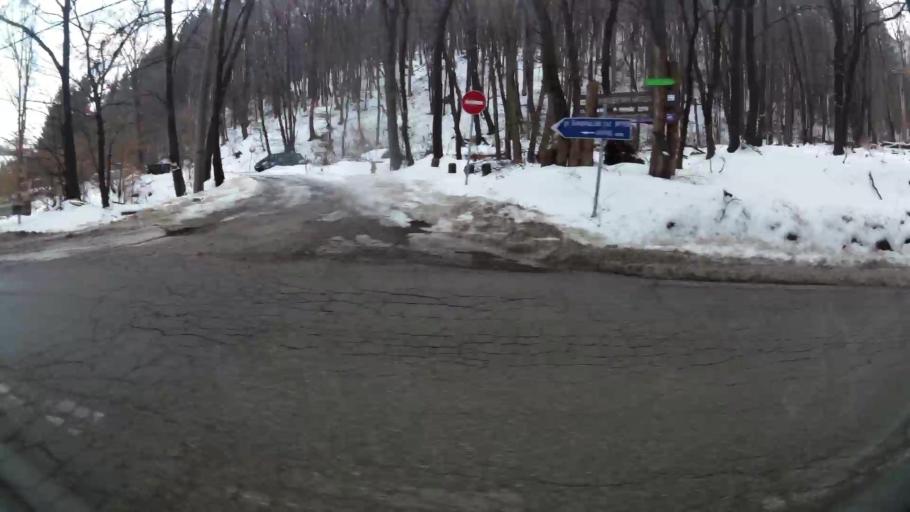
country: BG
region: Sofia-Capital
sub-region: Stolichna Obshtina
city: Sofia
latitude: 42.6457
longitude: 23.2498
